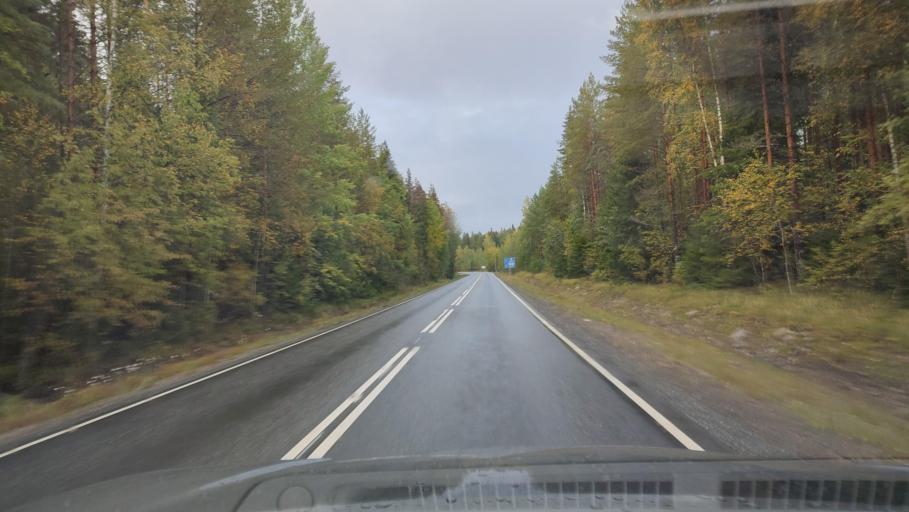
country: FI
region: Southern Ostrobothnia
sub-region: Suupohja
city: Karijoki
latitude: 62.2819
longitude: 21.6180
